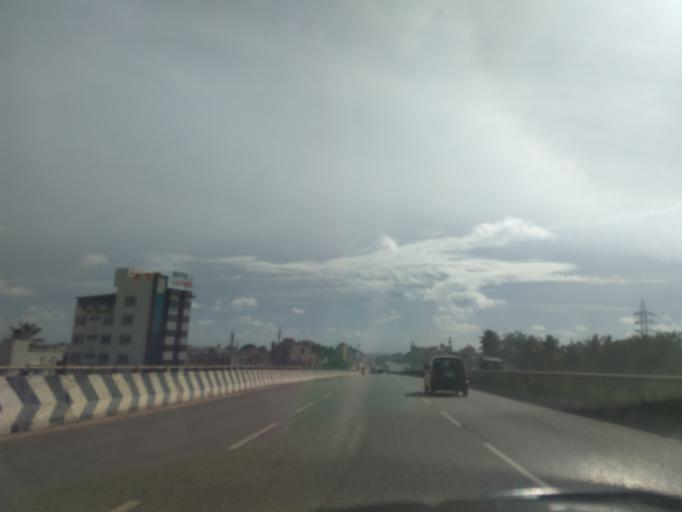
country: IN
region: Karnataka
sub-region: Bangalore Rural
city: Hoskote
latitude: 13.0728
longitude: 77.7880
